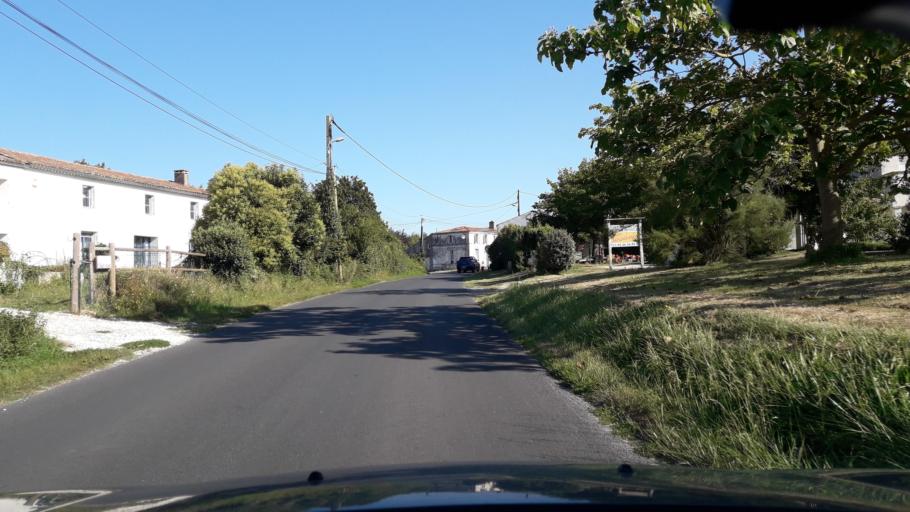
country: FR
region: Poitou-Charentes
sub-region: Departement de la Charente-Maritime
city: Etaules
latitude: 45.7109
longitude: -1.1128
